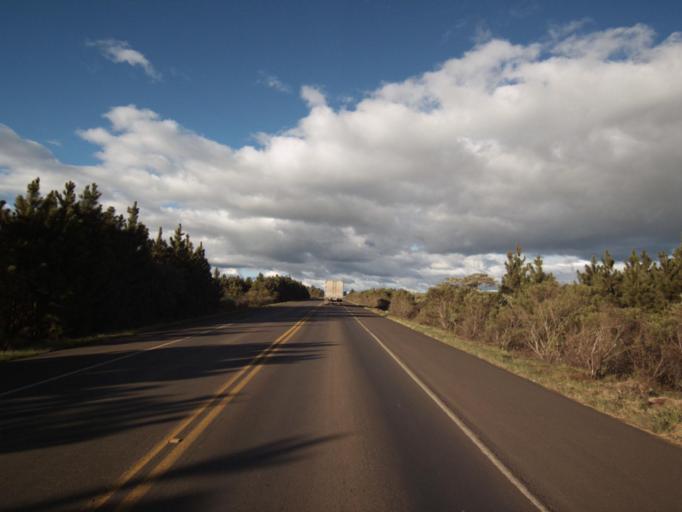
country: BR
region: Santa Catarina
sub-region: Campos Novos
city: Campos Novos
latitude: -27.3585
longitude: -51.2909
